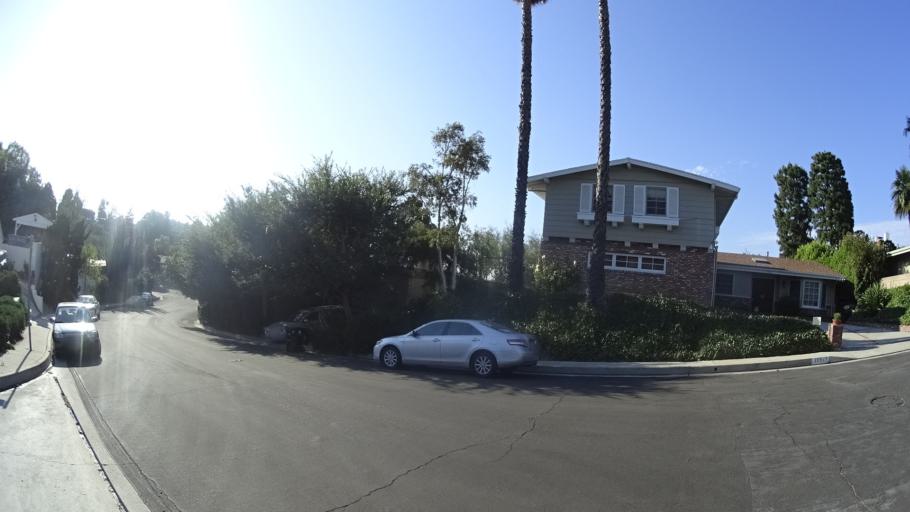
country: US
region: California
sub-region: Los Angeles County
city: Universal City
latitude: 34.1268
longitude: -118.3775
